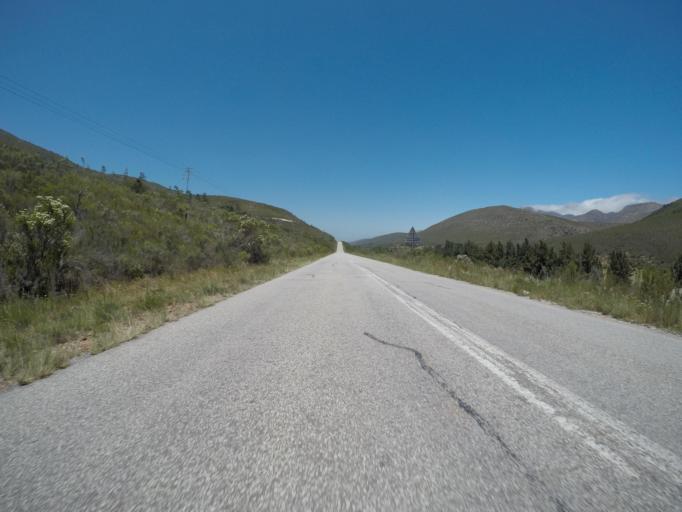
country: ZA
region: Eastern Cape
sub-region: Cacadu District Municipality
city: Kareedouw
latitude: -33.8646
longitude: 24.0083
